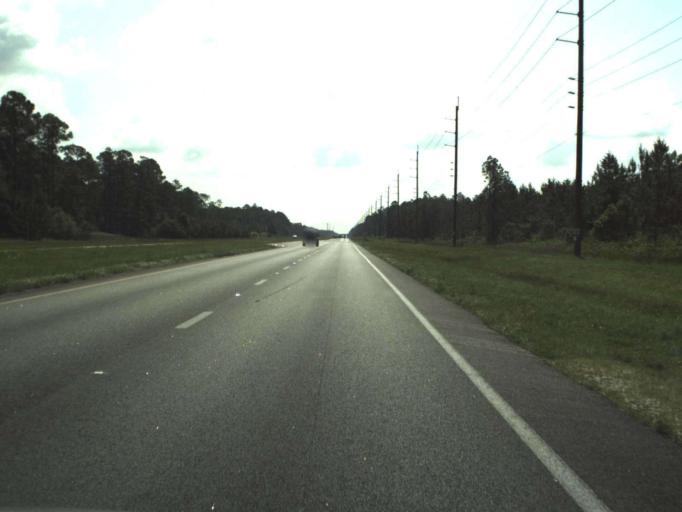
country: US
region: Florida
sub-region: Volusia County
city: Glencoe
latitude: 29.0120
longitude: -81.0181
